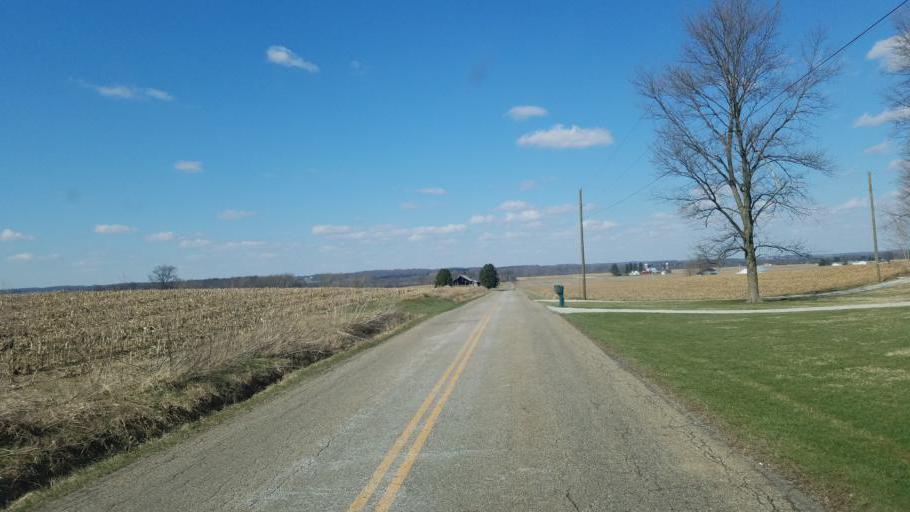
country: US
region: Ohio
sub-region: Knox County
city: Fredericktown
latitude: 40.4398
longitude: -82.5910
